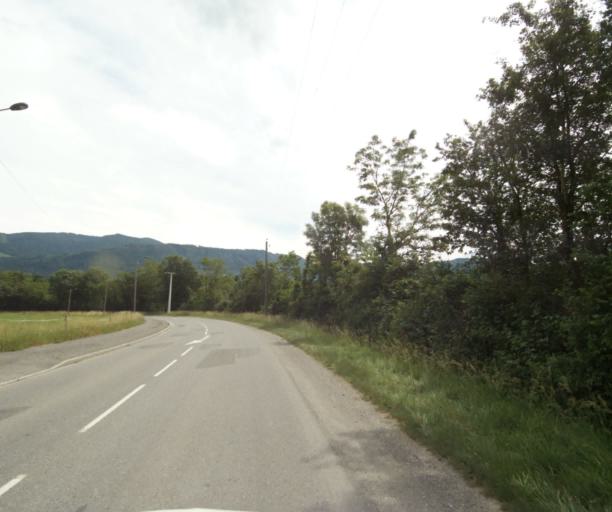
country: FR
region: Rhone-Alpes
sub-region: Departement de la Haute-Savoie
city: Perrignier
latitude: 46.3029
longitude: 6.4271
